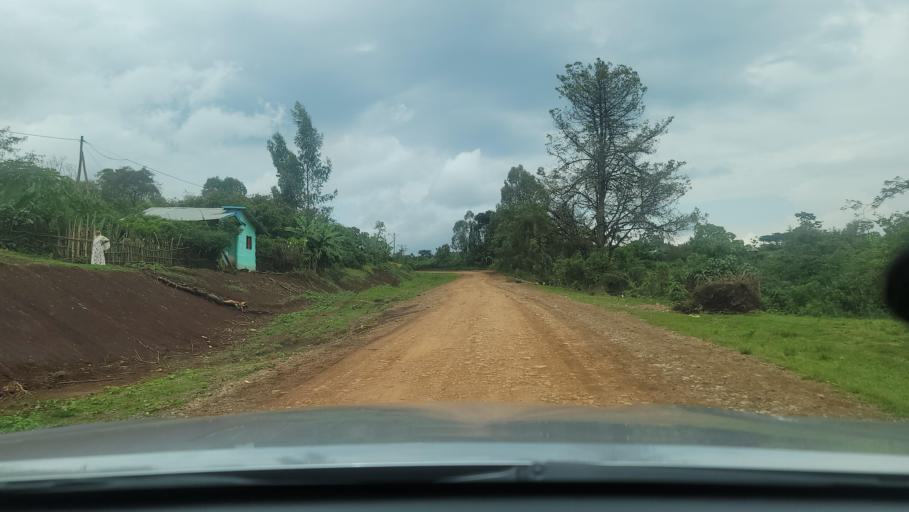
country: ET
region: Oromiya
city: Agaro
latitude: 7.7923
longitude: 36.4385
